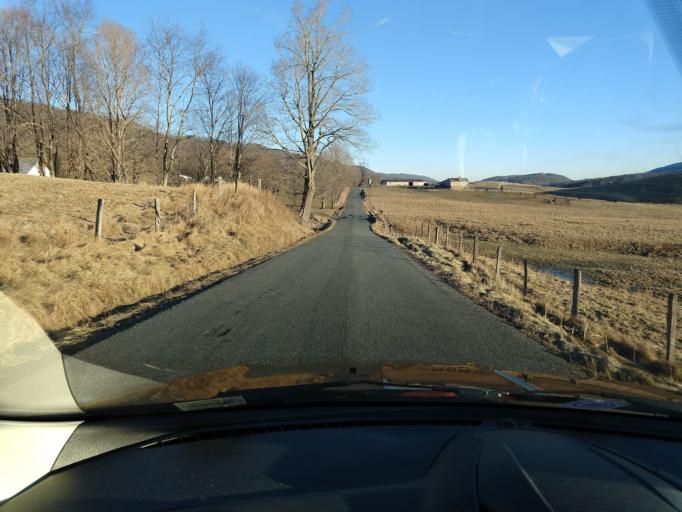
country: US
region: Virginia
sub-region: Highland County
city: Monterey
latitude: 38.3815
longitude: -79.6635
